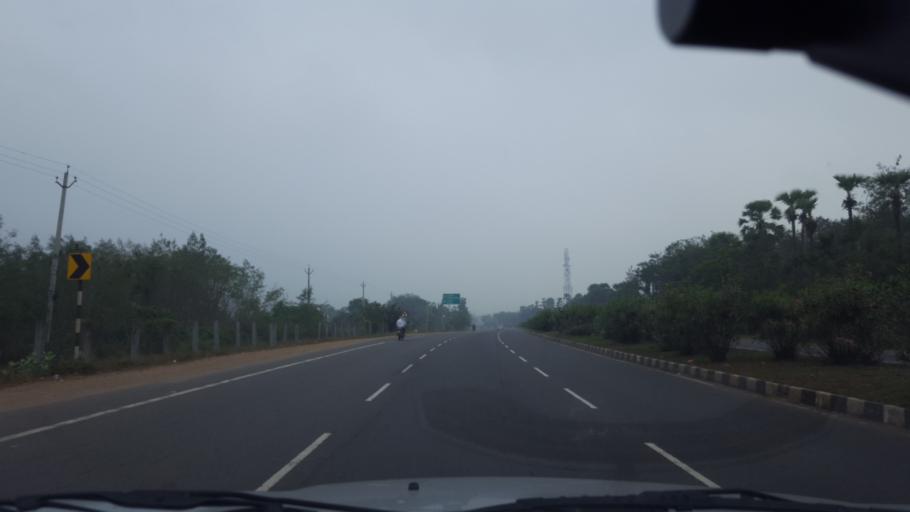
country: IN
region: Andhra Pradesh
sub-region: Prakasam
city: Addanki
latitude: 15.8346
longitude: 80.0476
